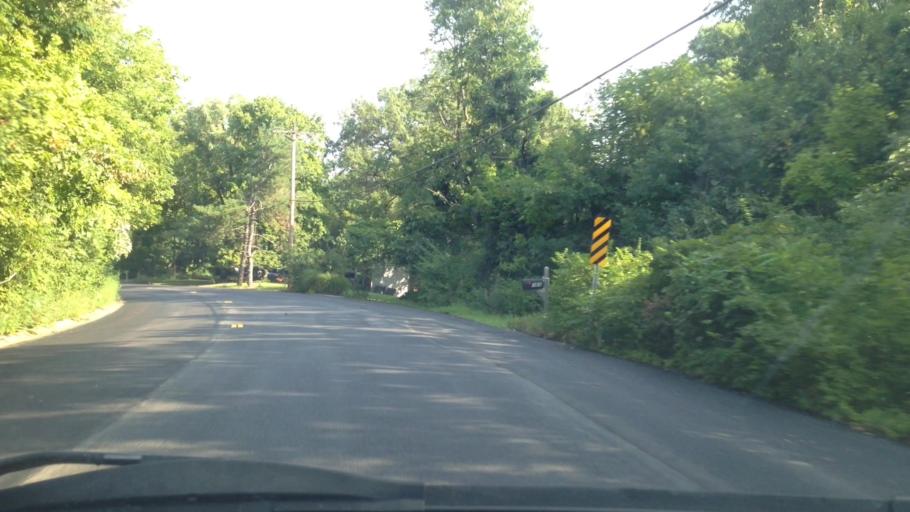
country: US
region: Missouri
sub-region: Saint Louis County
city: Des Peres
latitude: 38.5775
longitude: -90.4347
